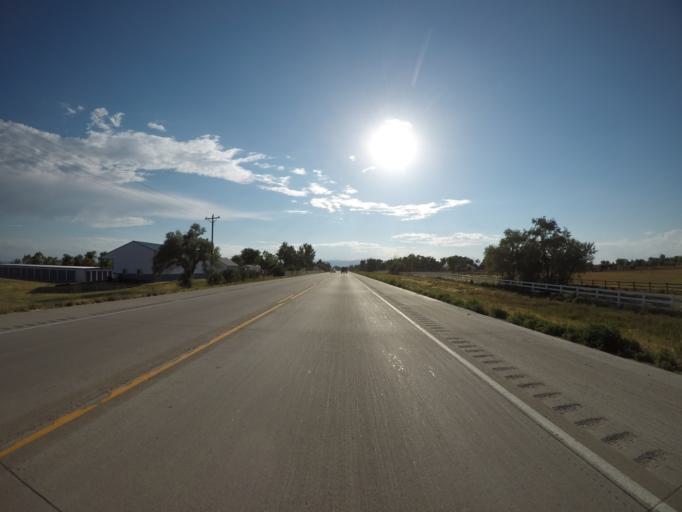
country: US
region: Colorado
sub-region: Weld County
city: Severance
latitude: 40.5816
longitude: -104.9196
